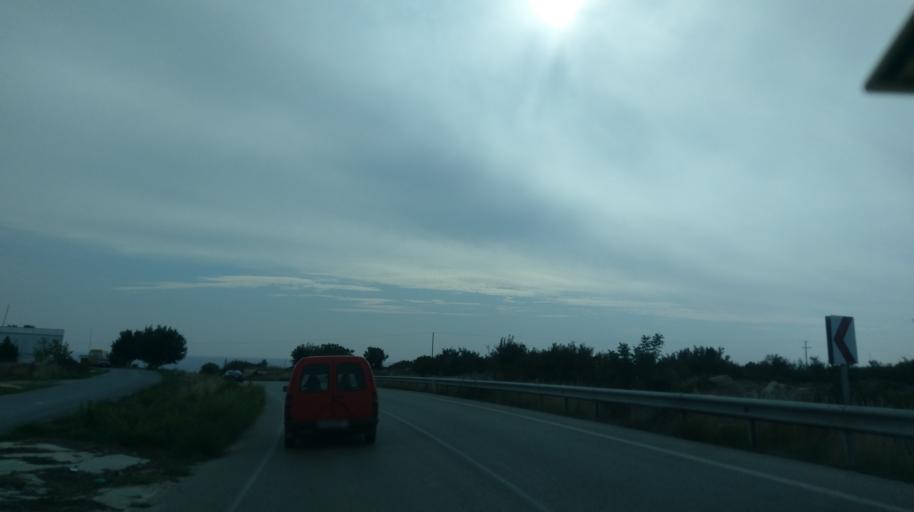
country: CY
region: Ammochostos
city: Leonarisso
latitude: 35.4313
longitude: 34.1279
